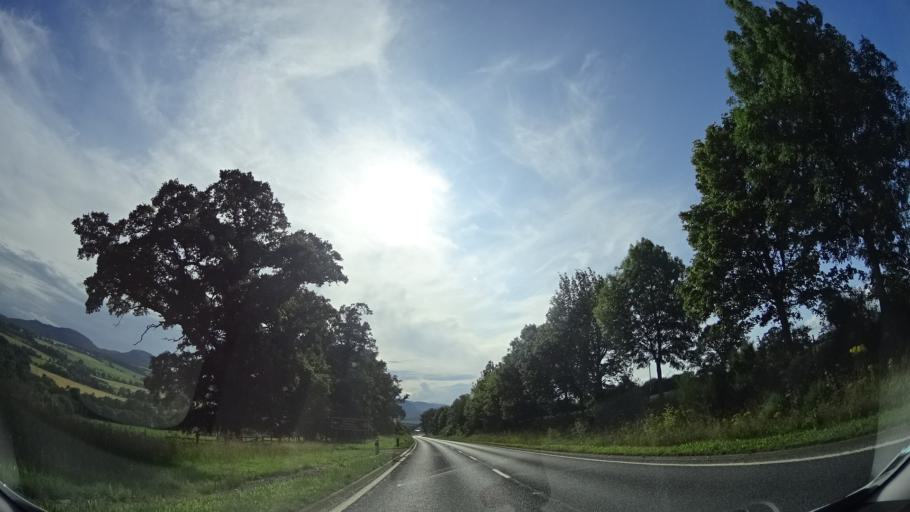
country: GB
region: Scotland
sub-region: Highland
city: Muir of Ord
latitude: 57.5585
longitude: -4.5307
